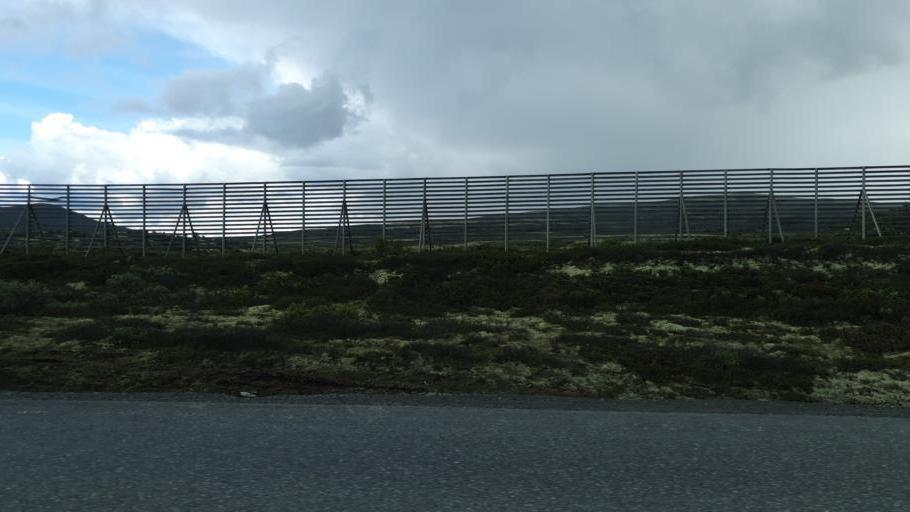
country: NO
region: Sor-Trondelag
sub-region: Oppdal
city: Oppdal
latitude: 62.2786
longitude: 9.5947
